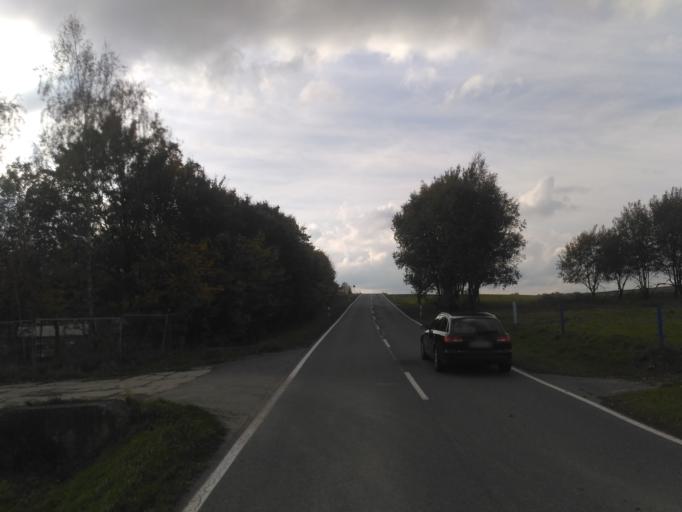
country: DE
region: Saxony
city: Neustadt in Sachsen
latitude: 50.9656
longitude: 14.2120
